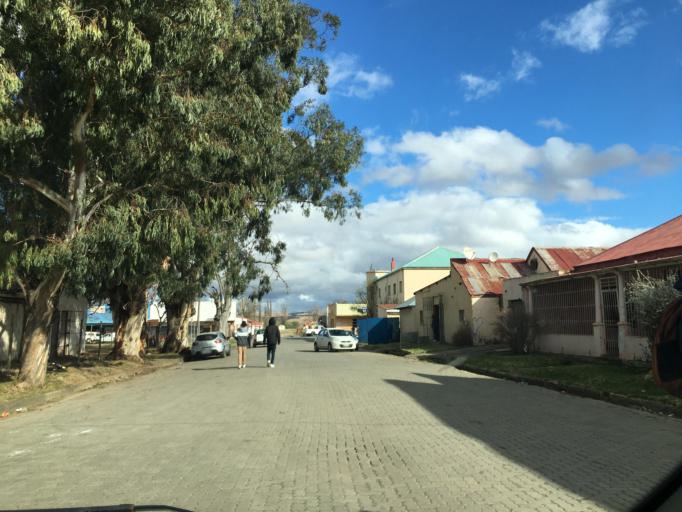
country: ZA
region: Eastern Cape
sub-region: Chris Hani District Municipality
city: Elliot
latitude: -31.3325
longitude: 27.8516
